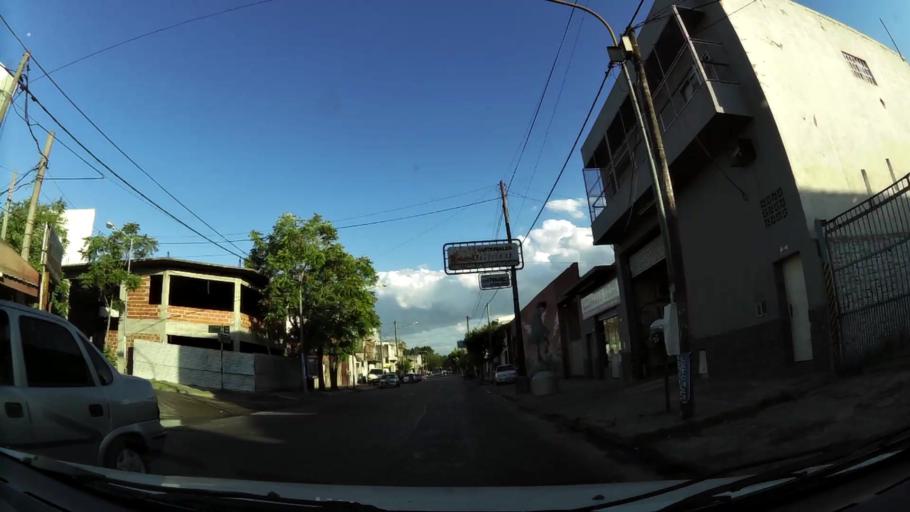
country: AR
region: Buenos Aires
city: Caseros
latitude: -34.5554
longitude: -58.5733
